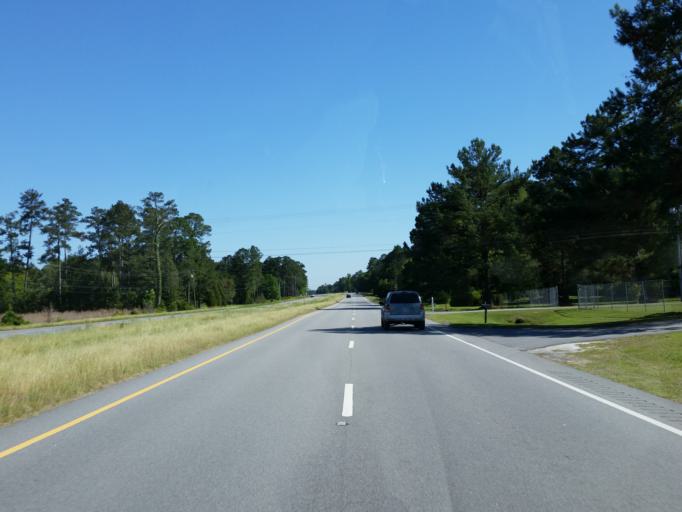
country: US
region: Georgia
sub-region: Lowndes County
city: Valdosta
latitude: 30.7213
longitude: -83.2164
